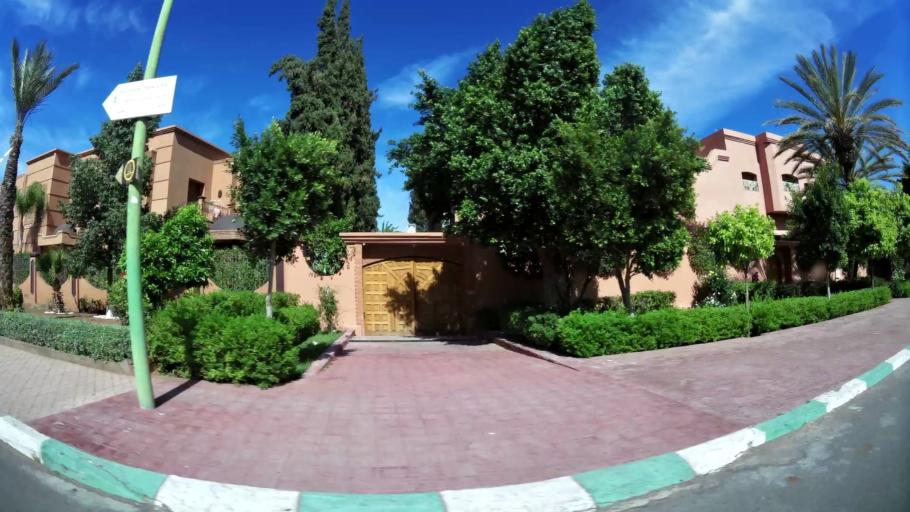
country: MA
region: Marrakech-Tensift-Al Haouz
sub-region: Marrakech
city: Marrakesh
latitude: 31.6428
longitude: -8.0469
